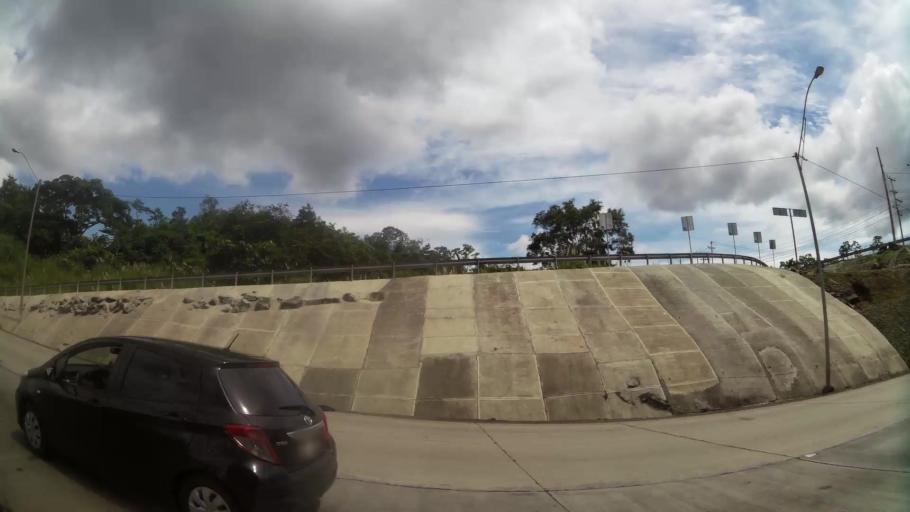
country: PA
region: Panama
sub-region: Distrito Arraijan
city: Arraijan
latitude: 8.9533
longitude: -79.6615
